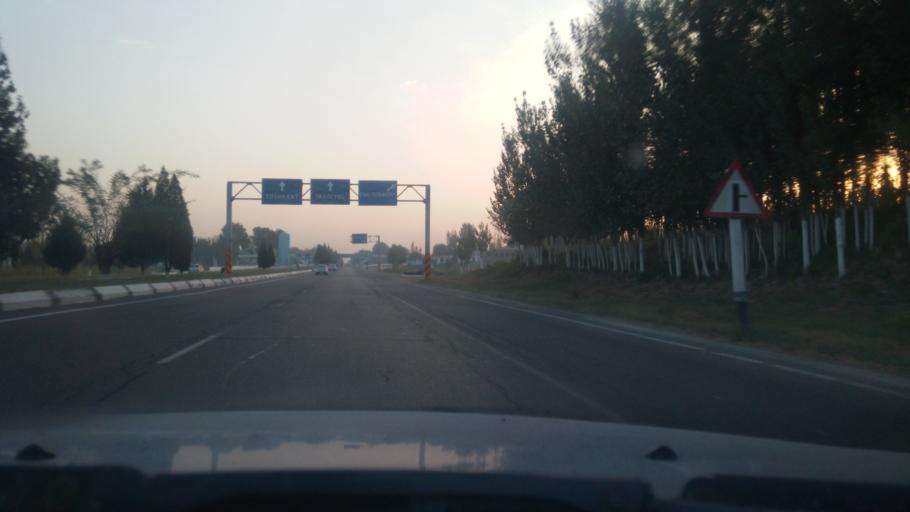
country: UZ
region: Toshkent
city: Amir Timur
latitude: 41.0493
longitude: 68.8938
